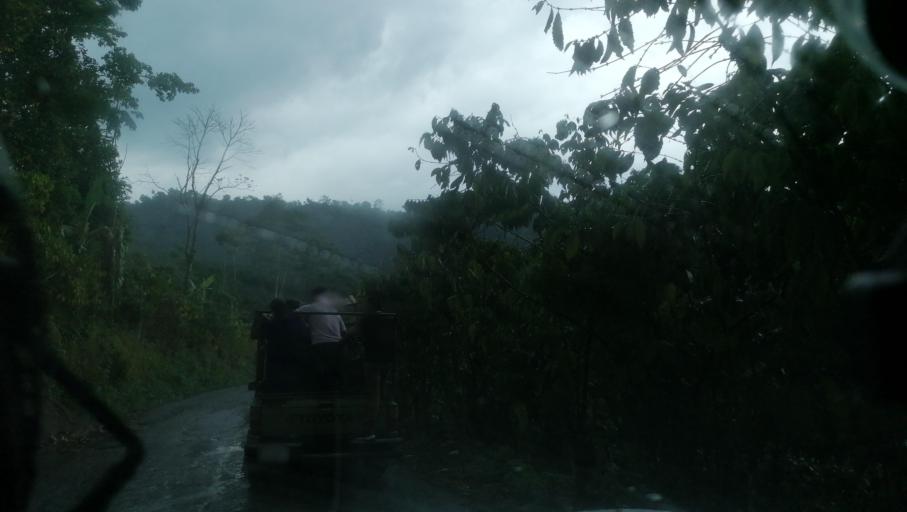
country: MX
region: Chiapas
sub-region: Cacahoatan
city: Benito Juarez
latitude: 15.0624
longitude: -92.1934
